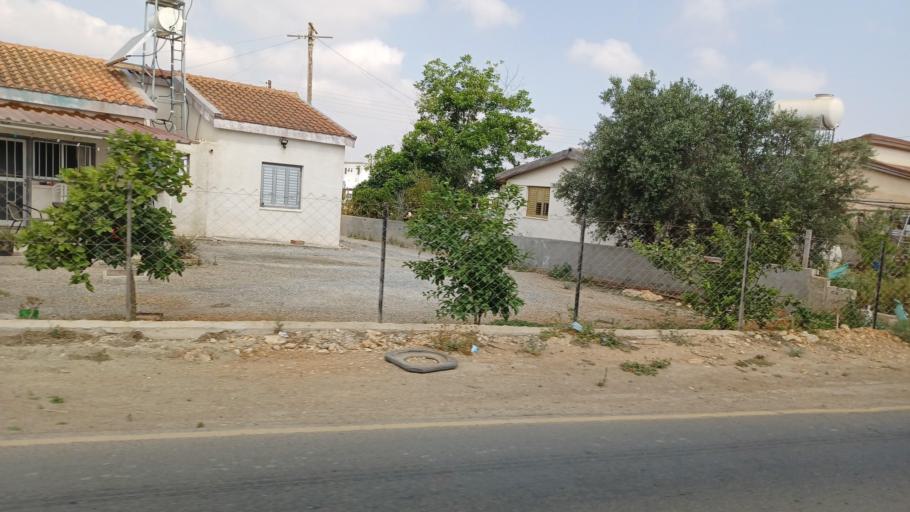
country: CY
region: Ammochostos
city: Deryneia
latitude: 35.0491
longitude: 33.9569
